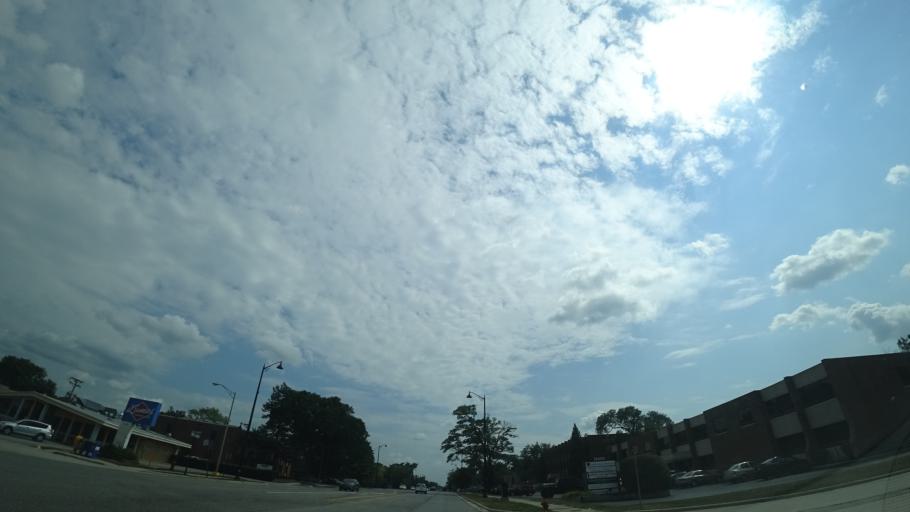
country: US
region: Illinois
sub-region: Cook County
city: Palos Heights
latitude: 41.6663
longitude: -87.7966
